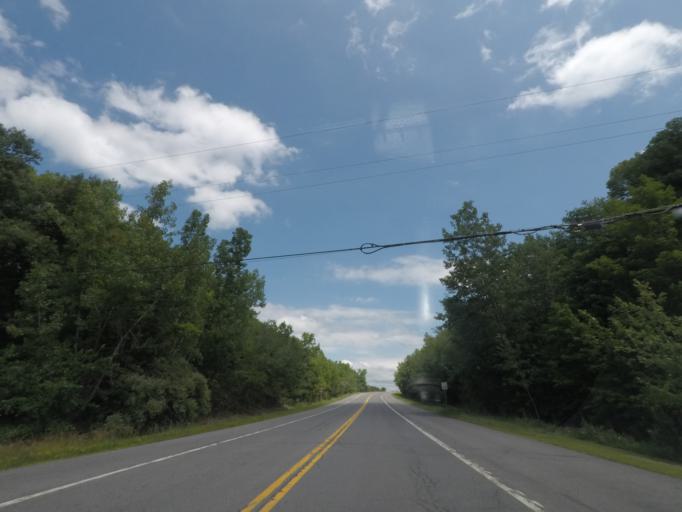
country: US
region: New York
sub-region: Rensselaer County
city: East Greenbush
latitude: 42.5515
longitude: -73.6824
